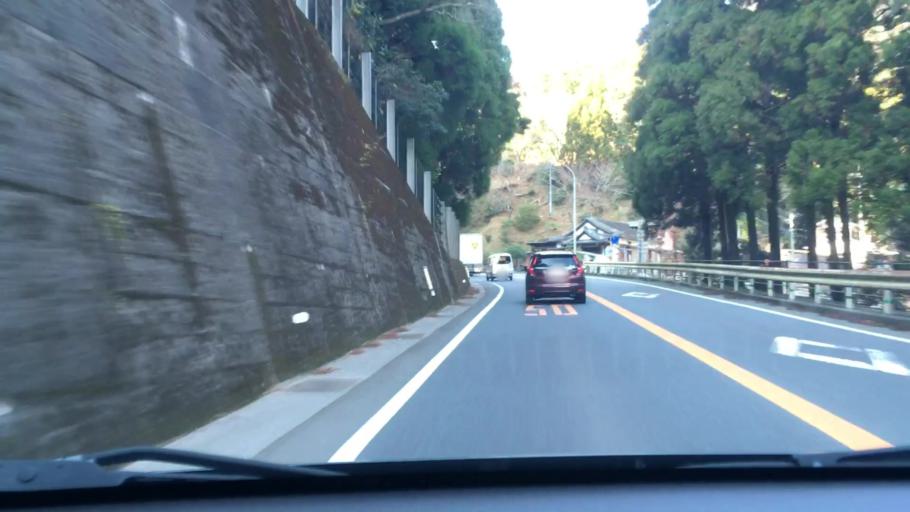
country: JP
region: Oita
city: Tsukumiura
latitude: 32.9998
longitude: 131.8136
